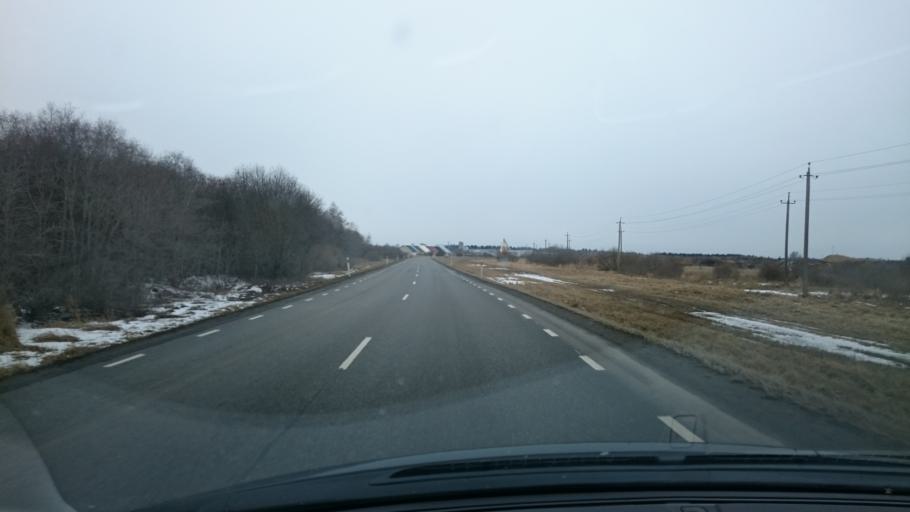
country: EE
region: Harju
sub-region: Harku vald
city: Tabasalu
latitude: 59.3978
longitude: 24.5521
